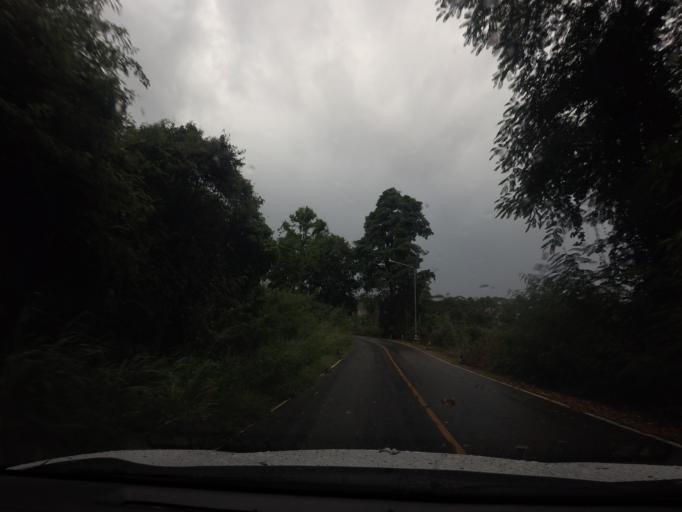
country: TH
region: Rayong
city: Ban Chang
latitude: 12.7610
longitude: 100.9560
